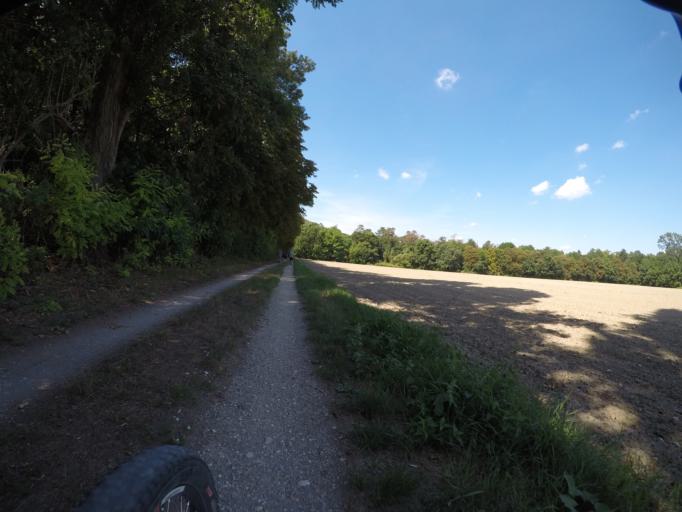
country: AT
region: Lower Austria
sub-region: Politischer Bezirk Ganserndorf
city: Gross-Enzersdorf
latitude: 48.1820
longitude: 16.5061
